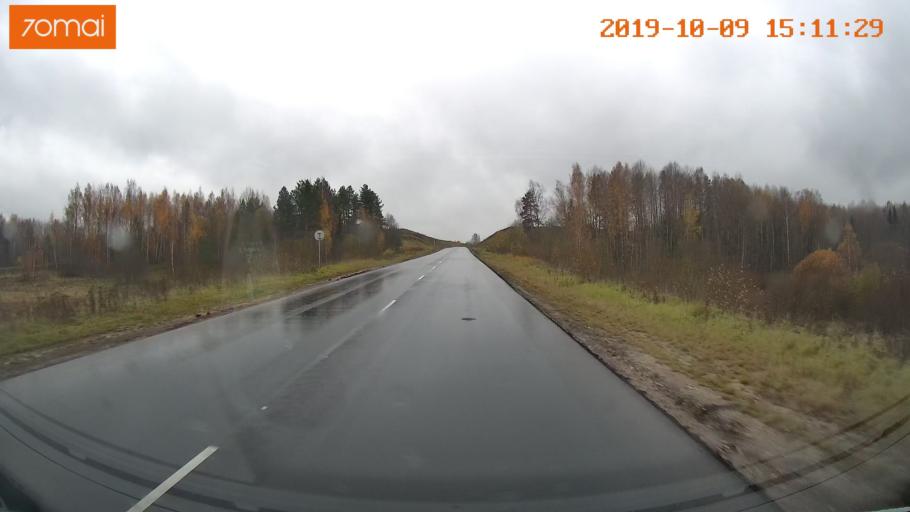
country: RU
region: Kostroma
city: Susanino
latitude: 58.1642
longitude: 41.6296
